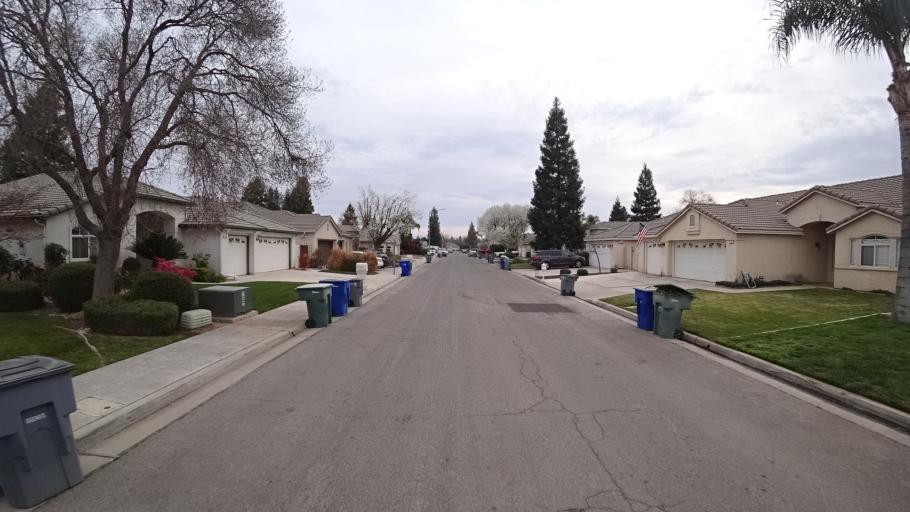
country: US
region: California
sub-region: Fresno County
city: Clovis
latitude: 36.8547
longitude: -119.7421
